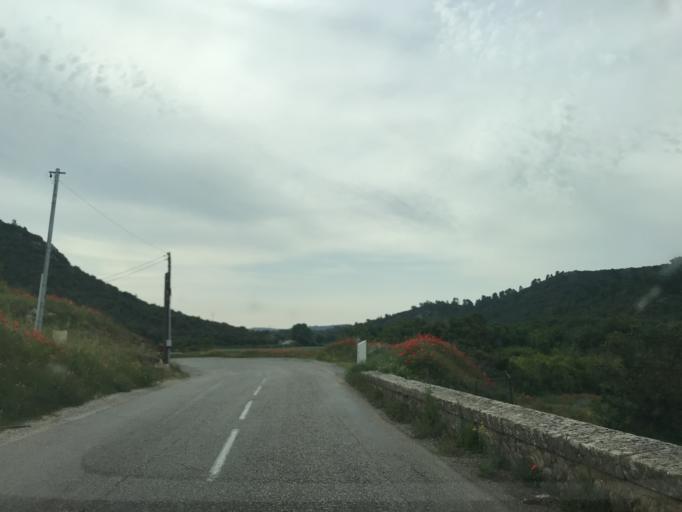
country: FR
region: Provence-Alpes-Cote d'Azur
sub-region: Departement du Vaucluse
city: Beaumont-de-Pertuis
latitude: 43.6810
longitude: 5.7177
